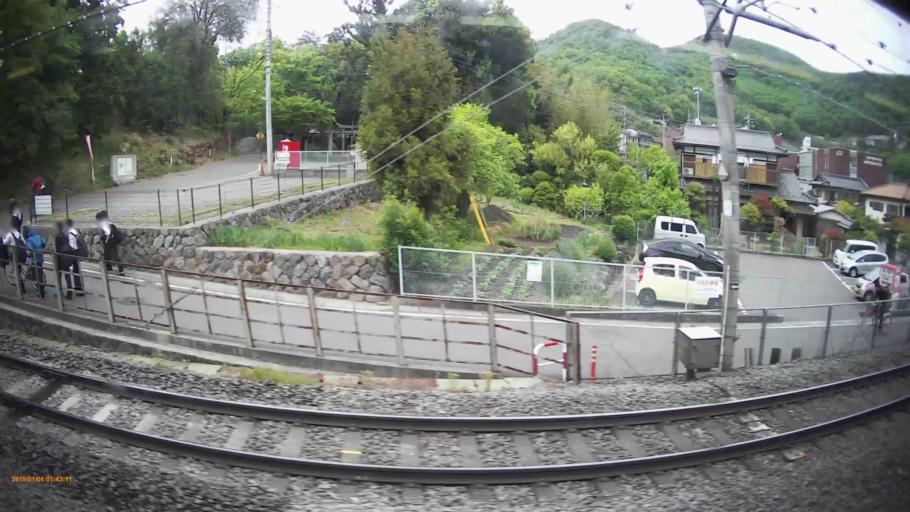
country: JP
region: Yamanashi
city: Kofu-shi
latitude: 35.6601
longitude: 138.5966
